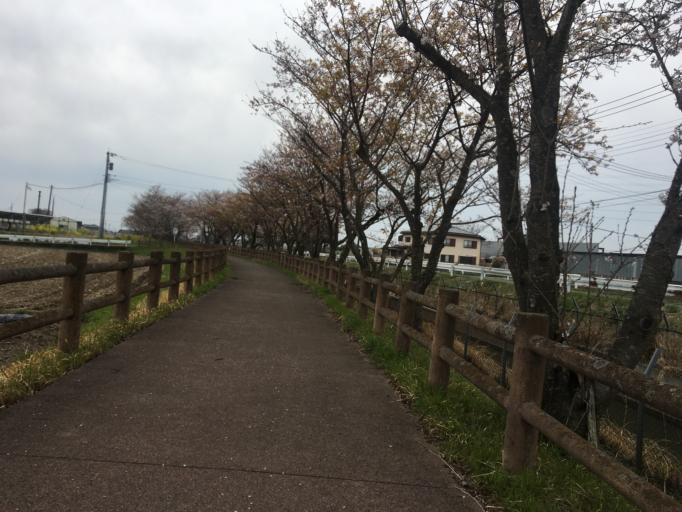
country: JP
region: Saitama
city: Konosu
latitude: 36.1101
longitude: 139.5359
